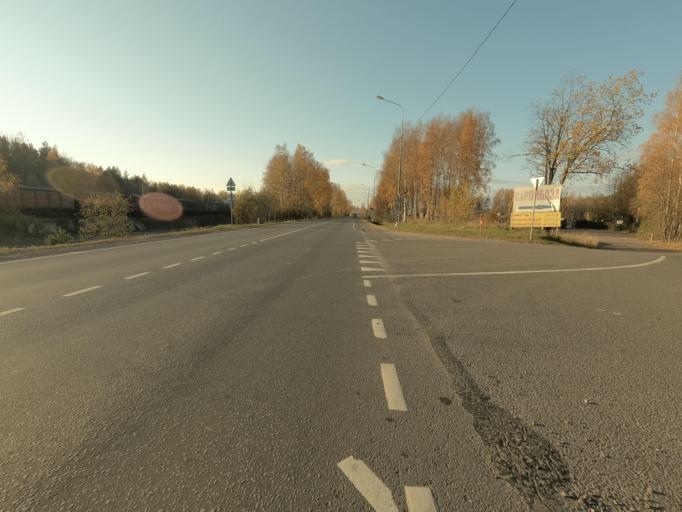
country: RU
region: Leningrad
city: Kirovsk
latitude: 59.8569
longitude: 31.0107
